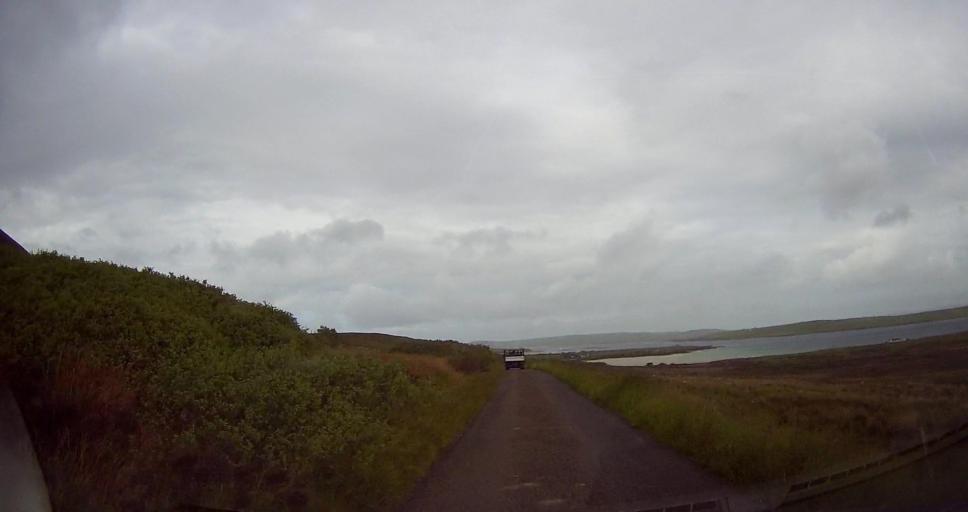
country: GB
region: Scotland
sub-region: Orkney Islands
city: Stromness
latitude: 58.8992
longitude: -3.3148
